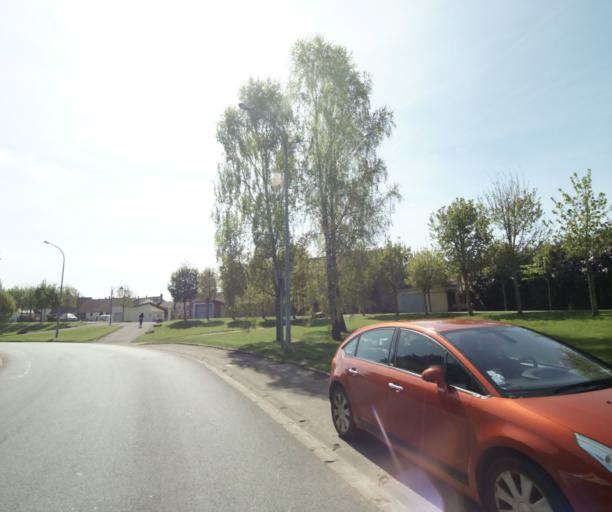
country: FR
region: Ile-de-France
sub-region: Departement de Seine-et-Marne
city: Nangis
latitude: 48.5569
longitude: 3.0170
